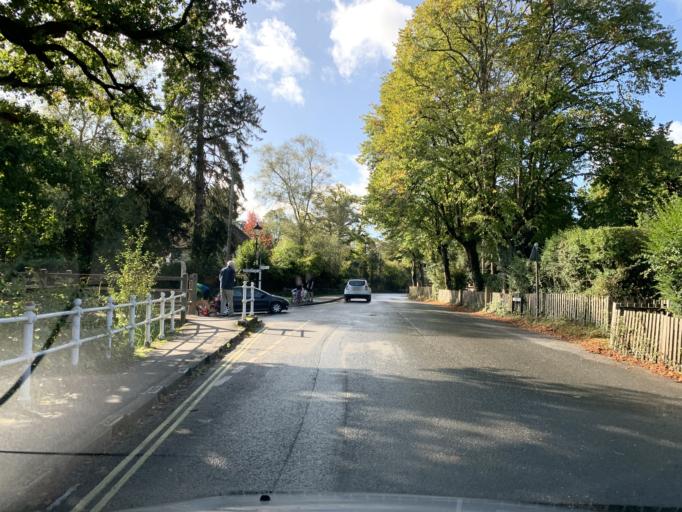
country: GB
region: England
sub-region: Hampshire
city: Brockenhurst
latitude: 50.8196
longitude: -1.5798
